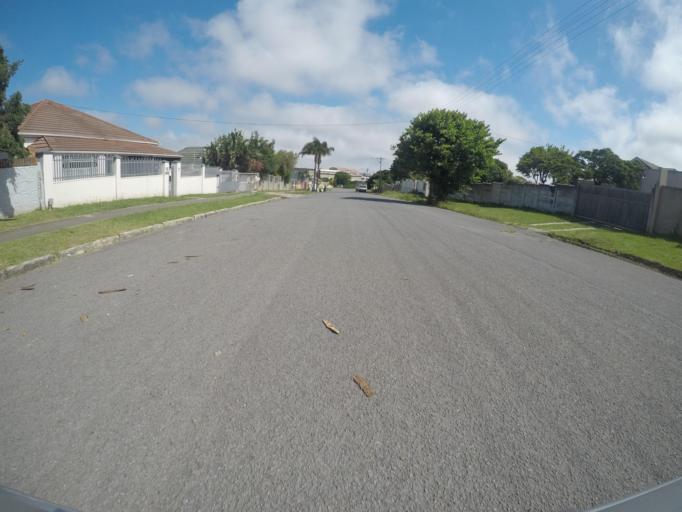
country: ZA
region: Eastern Cape
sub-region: Buffalo City Metropolitan Municipality
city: East London
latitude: -32.9793
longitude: 27.8907
